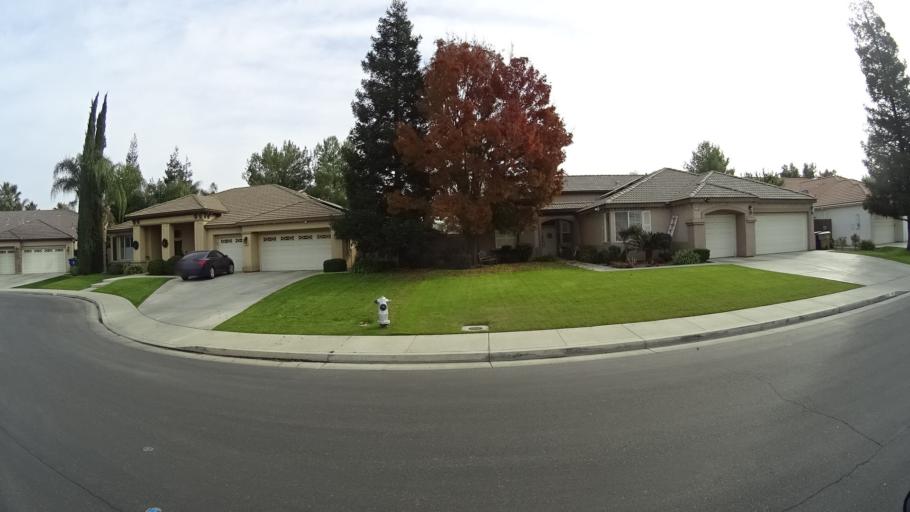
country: US
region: California
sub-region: Kern County
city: Rosedale
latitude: 35.3460
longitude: -119.1349
